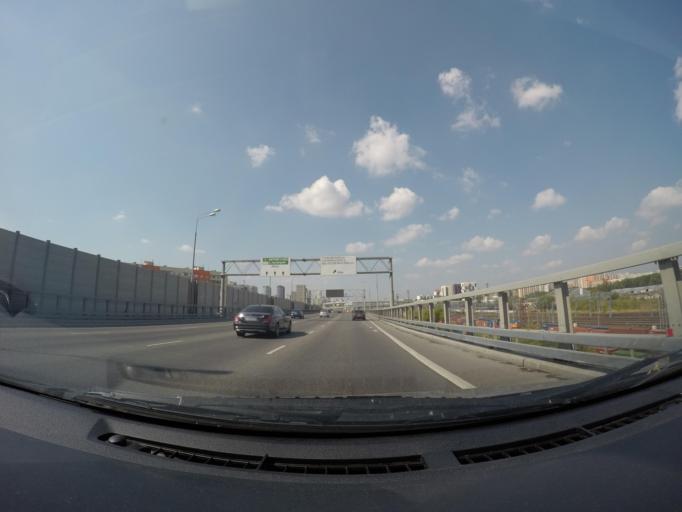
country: RU
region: Moscow
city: Zapadnoye Degunino
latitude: 55.8636
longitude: 37.5208
